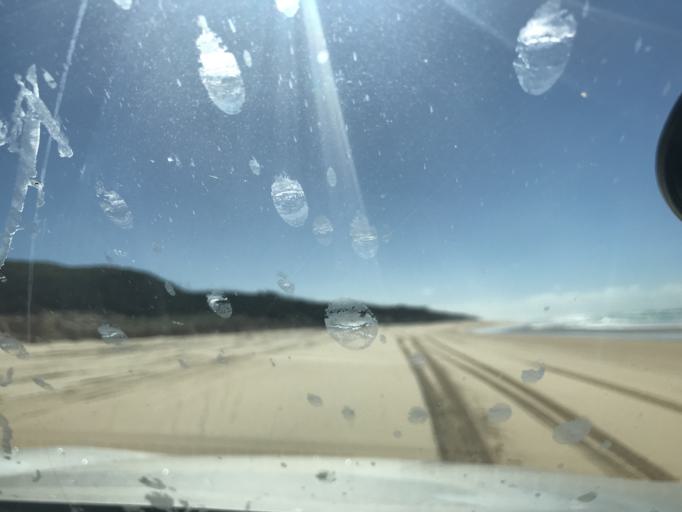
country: AU
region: Queensland
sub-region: Fraser Coast
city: Urangan
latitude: -25.0454
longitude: 153.3432
